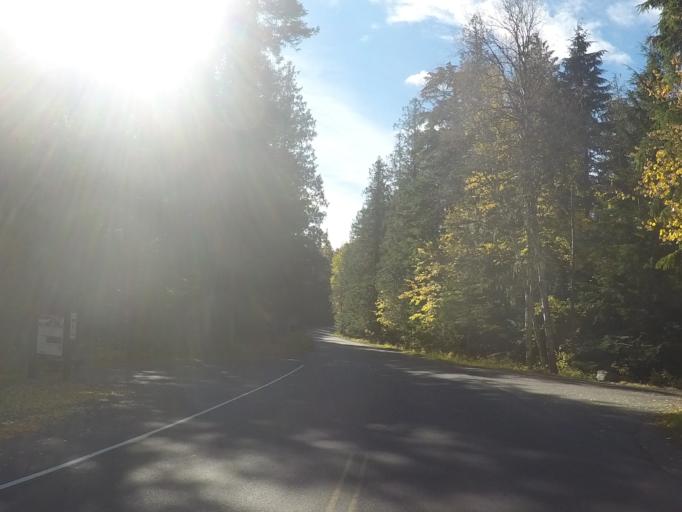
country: US
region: Montana
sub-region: Flathead County
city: Columbia Falls
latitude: 48.6063
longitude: -113.8845
